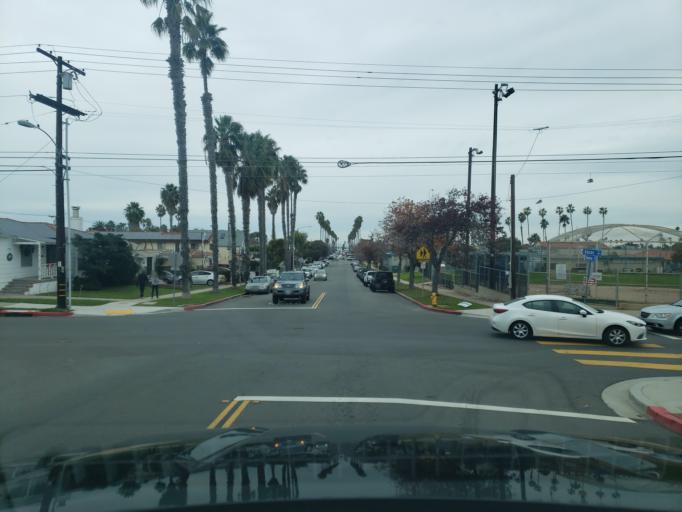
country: US
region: California
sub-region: San Diego County
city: Coronado
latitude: 32.7436
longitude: -117.2457
